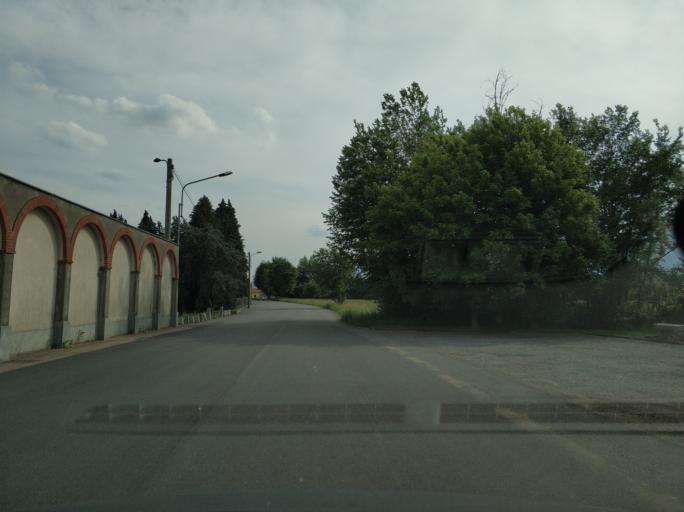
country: IT
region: Piedmont
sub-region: Provincia di Torino
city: Mathi
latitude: 45.2639
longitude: 7.5469
